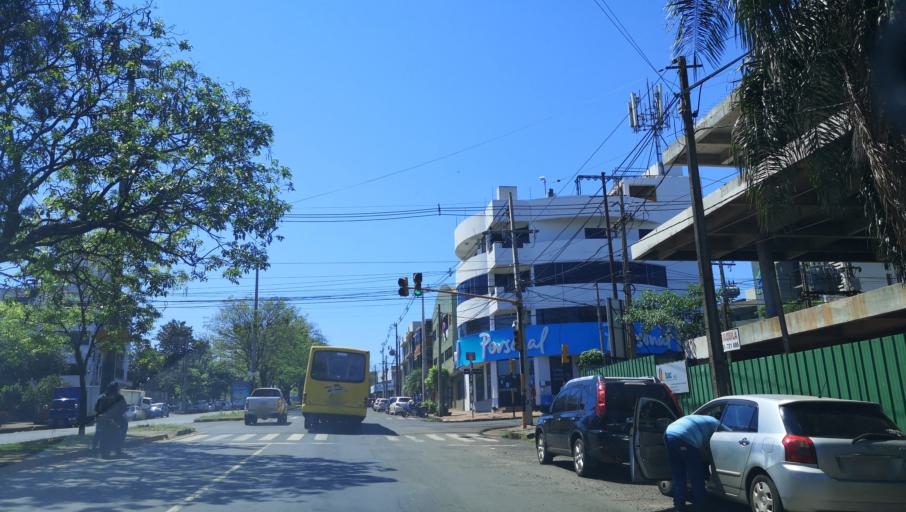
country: PY
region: Itapua
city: Encarnacion
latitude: -27.3267
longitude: -55.8705
